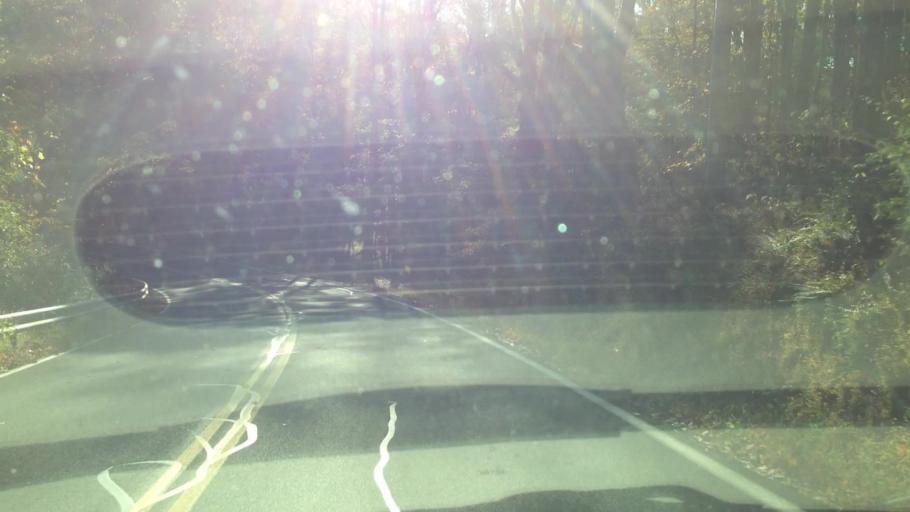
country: US
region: New York
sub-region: Dutchess County
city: Hyde Park
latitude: 41.8238
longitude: -73.9856
